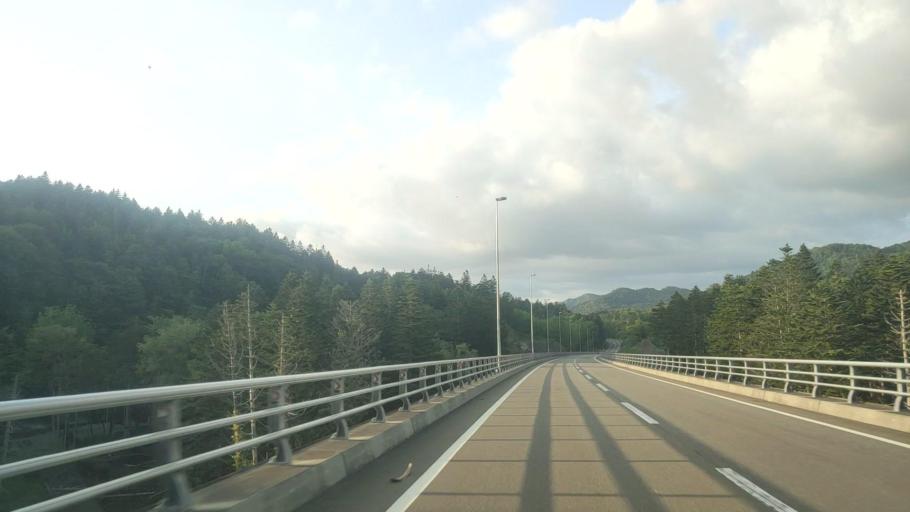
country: JP
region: Hokkaido
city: Bibai
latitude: 43.1074
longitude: 142.0981
